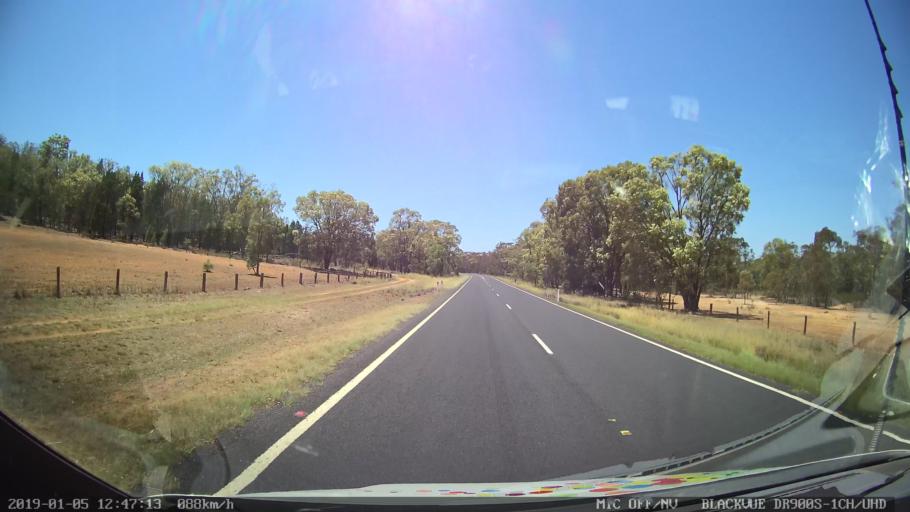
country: AU
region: New South Wales
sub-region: Warrumbungle Shire
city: Coonabarabran
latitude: -31.1168
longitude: 149.5734
